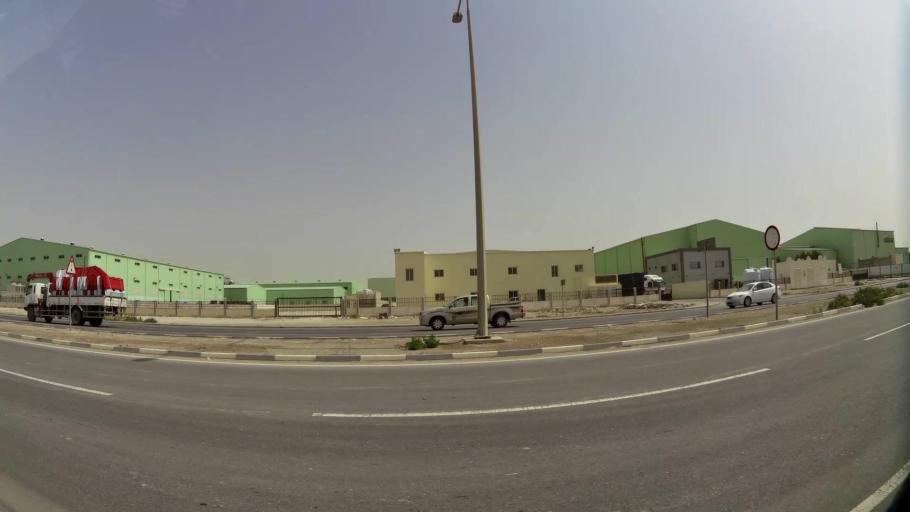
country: QA
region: Al Wakrah
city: Al Wukayr
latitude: 25.1580
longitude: 51.4096
